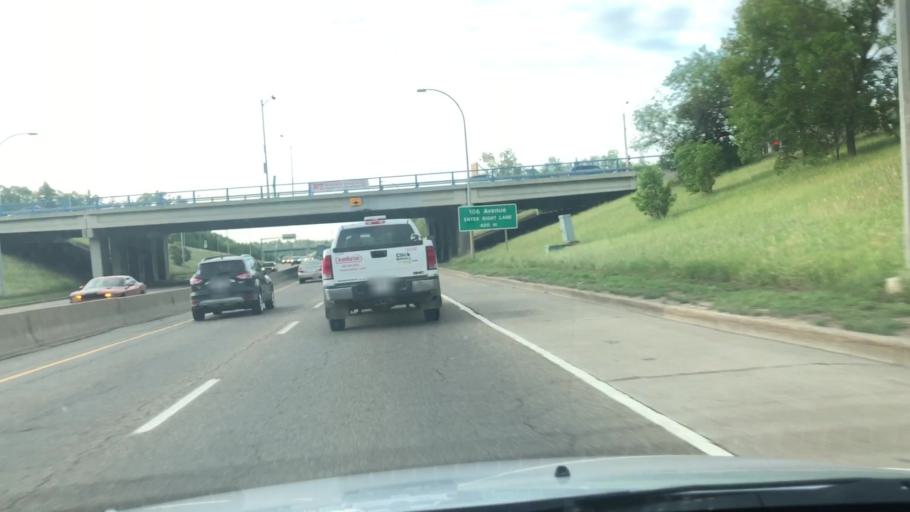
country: CA
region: Alberta
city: Edmonton
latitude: 53.5634
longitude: -113.4474
